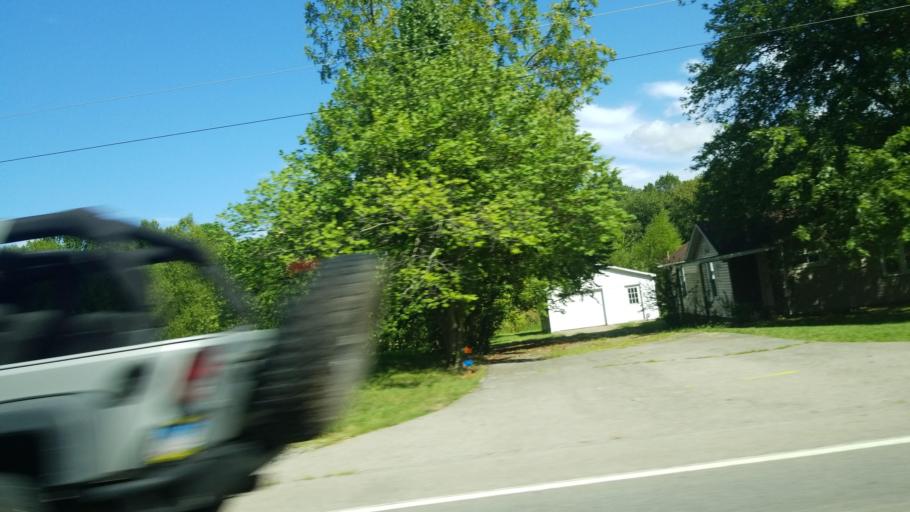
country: US
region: Illinois
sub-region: Williamson County
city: Marion
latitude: 37.7602
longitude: -88.9328
